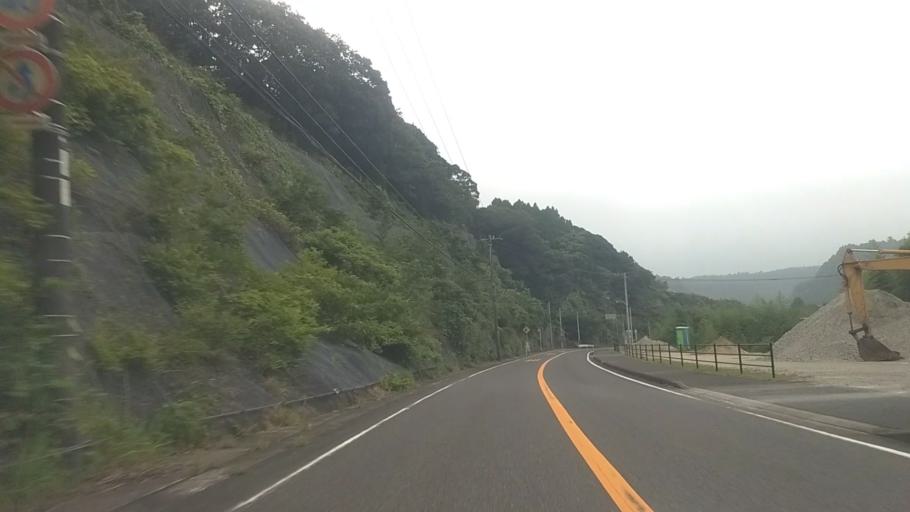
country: JP
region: Chiba
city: Katsuura
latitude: 35.2450
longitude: 140.2368
